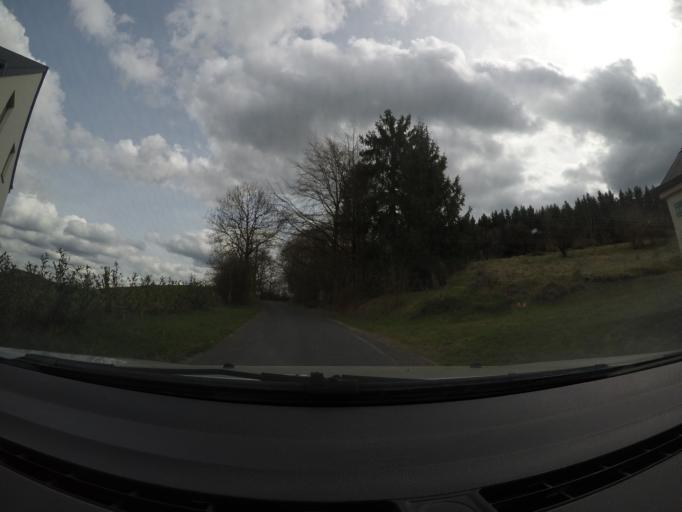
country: BE
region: Wallonia
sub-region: Province du Luxembourg
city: Leglise
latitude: 49.7970
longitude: 5.5375
